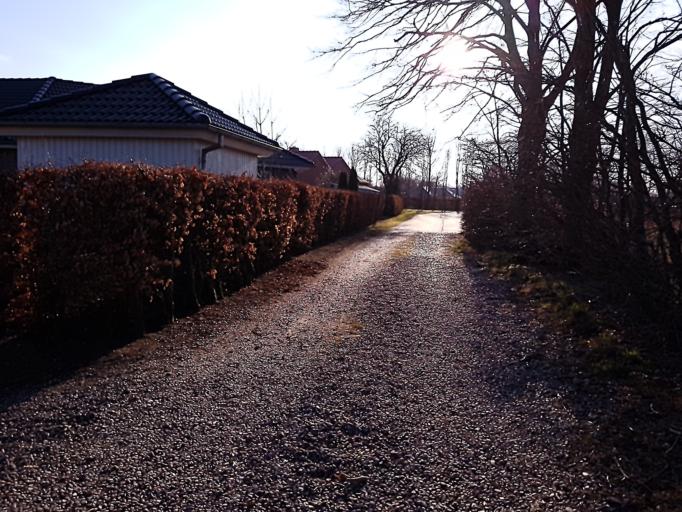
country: DK
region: South Denmark
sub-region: Esbjerg Kommune
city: Bramming
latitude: 55.4779
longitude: 8.6952
